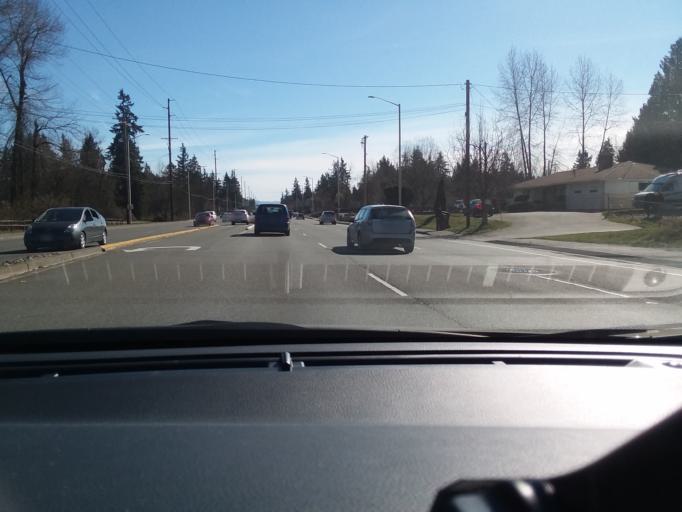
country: US
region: Washington
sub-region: Pierce County
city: Frederickson
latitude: 47.1216
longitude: -122.3576
